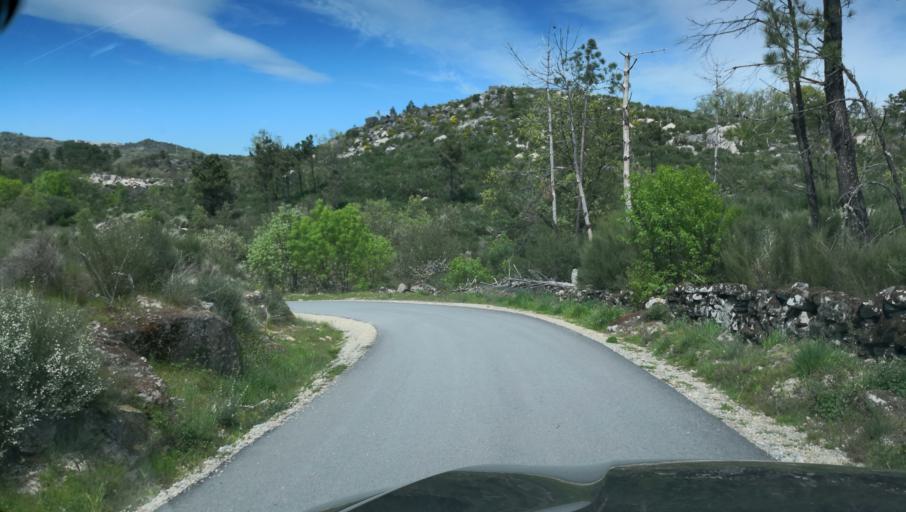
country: PT
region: Vila Real
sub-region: Vila Real
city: Vila Real
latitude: 41.3657
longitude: -7.6696
